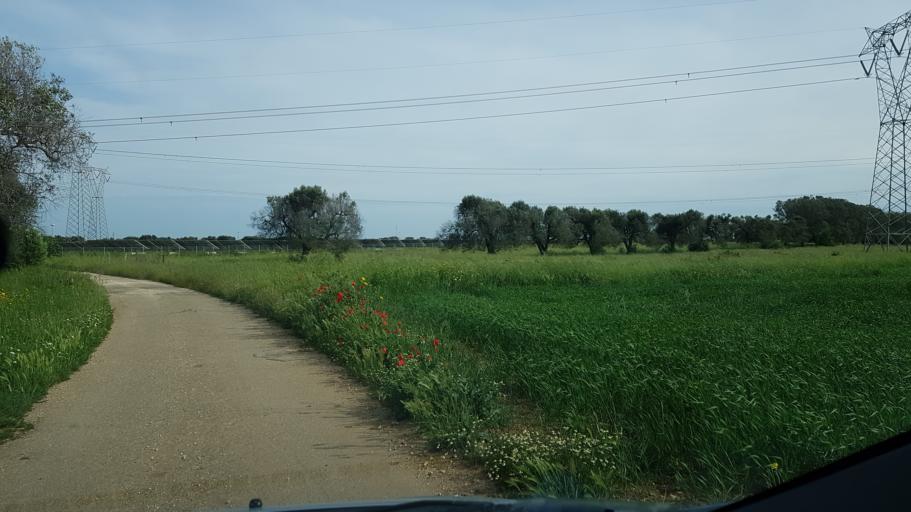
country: IT
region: Apulia
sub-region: Provincia di Brindisi
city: Tuturano
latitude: 40.5545
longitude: 17.9275
